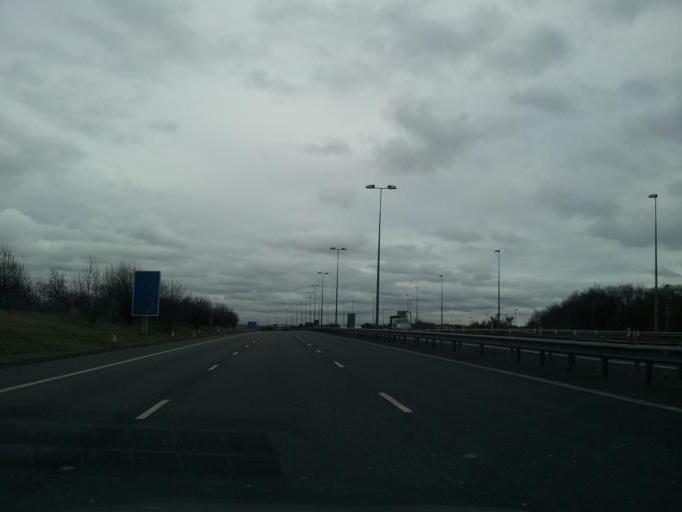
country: GB
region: England
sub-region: Staffordshire
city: Featherstone
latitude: 52.6687
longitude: -2.0721
